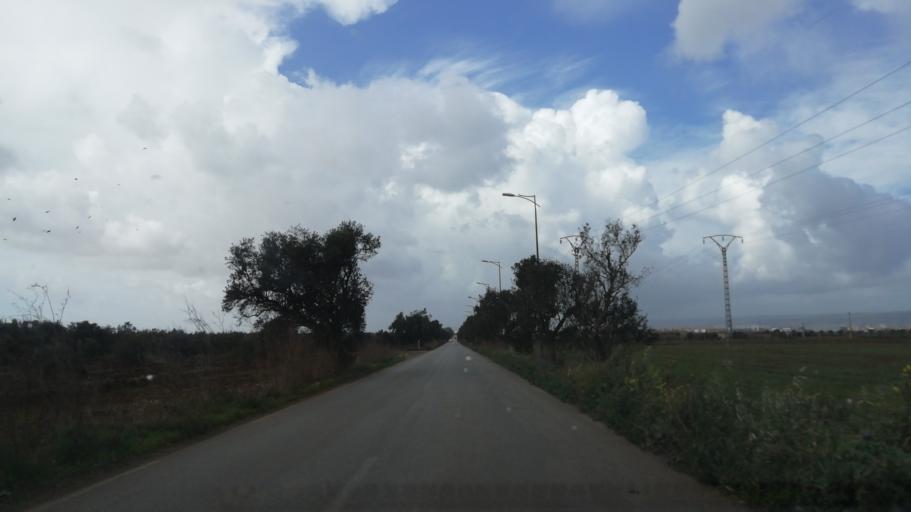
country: DZ
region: Oran
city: Sidi ech Chahmi
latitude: 35.6226
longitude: -0.5545
